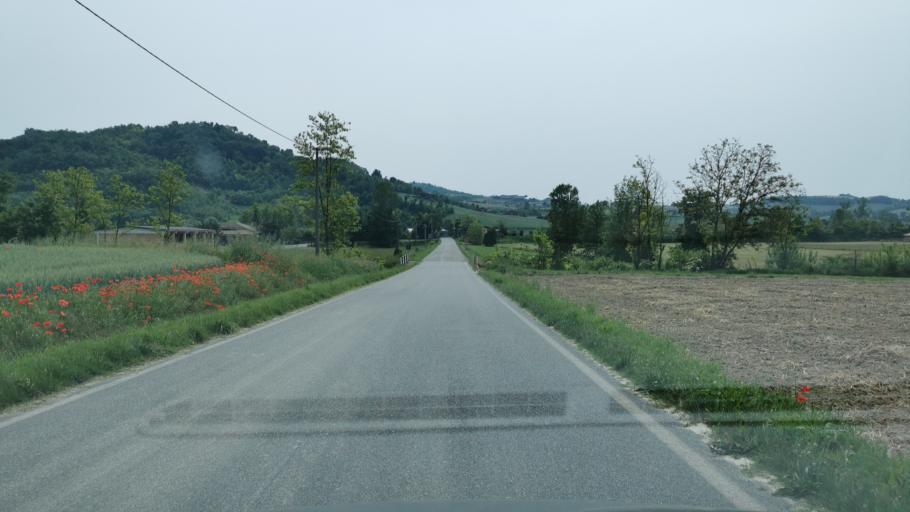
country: IT
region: Piedmont
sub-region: Provincia di Asti
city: Moncalvo
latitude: 45.0660
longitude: 8.2768
